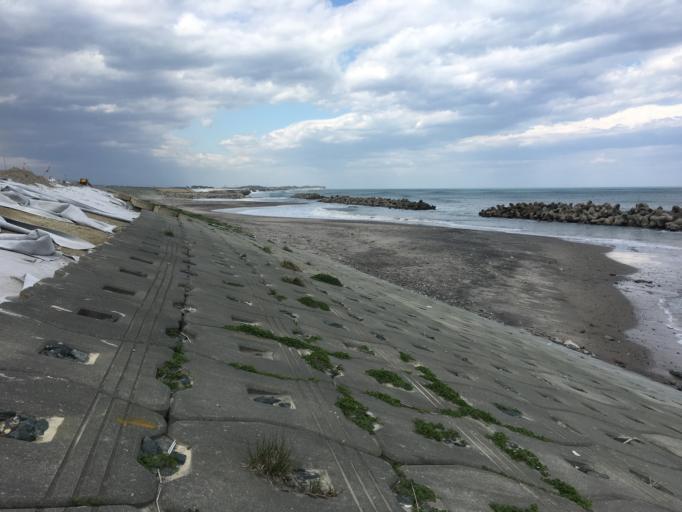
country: JP
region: Miyagi
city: Marumori
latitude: 37.7691
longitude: 140.9902
